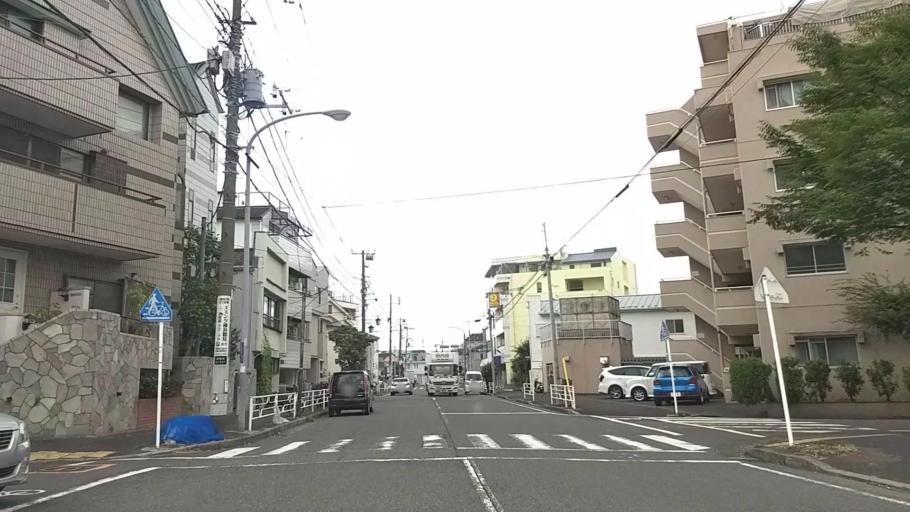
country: JP
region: Kanagawa
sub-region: Kawasaki-shi
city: Kawasaki
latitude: 35.5041
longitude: 139.6894
